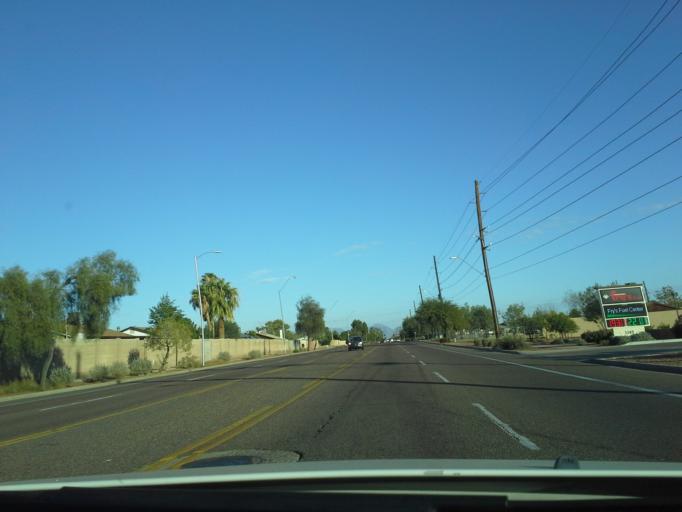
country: US
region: Arizona
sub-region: Maricopa County
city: Glendale
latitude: 33.6546
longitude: -112.0894
